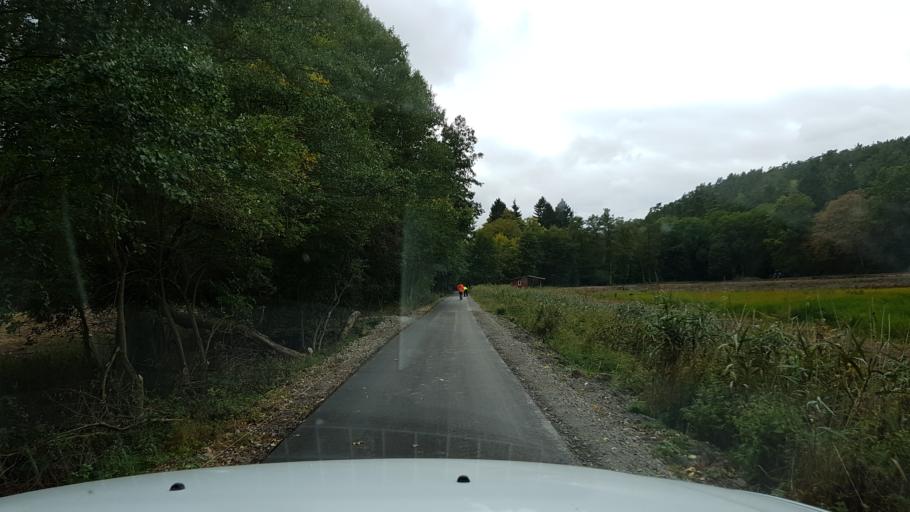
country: PL
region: West Pomeranian Voivodeship
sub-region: Powiat gryfinski
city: Cedynia
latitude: 52.8311
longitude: 14.2480
